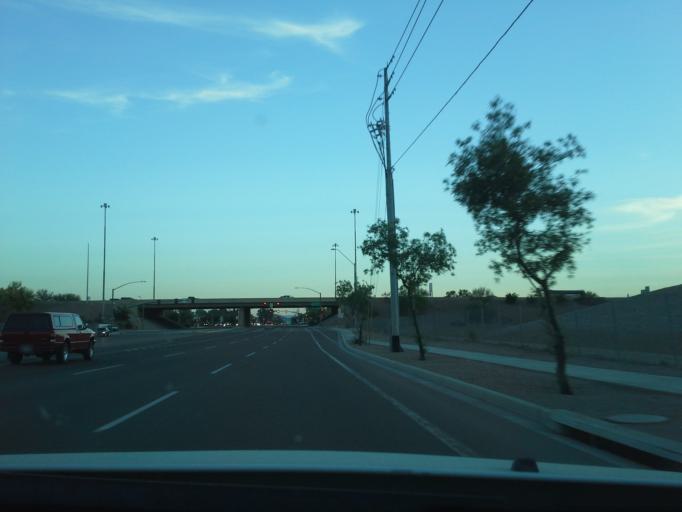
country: US
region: Arizona
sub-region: Maricopa County
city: Glendale
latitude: 33.6711
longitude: -112.0659
